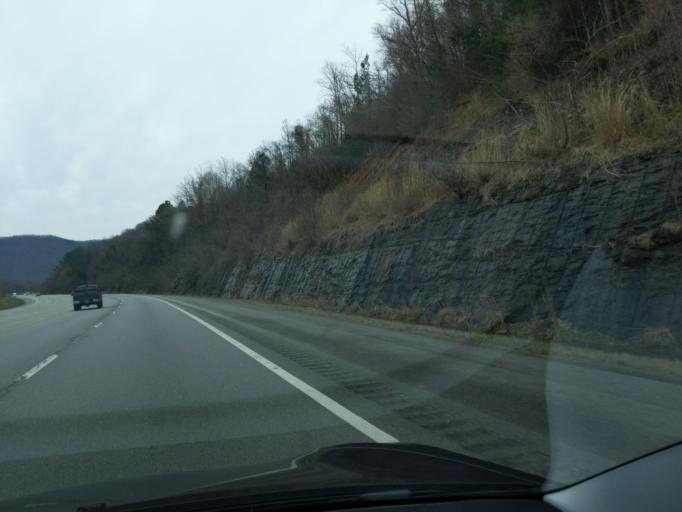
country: US
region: Kentucky
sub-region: Bell County
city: Pineville
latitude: 36.7712
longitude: -83.7275
